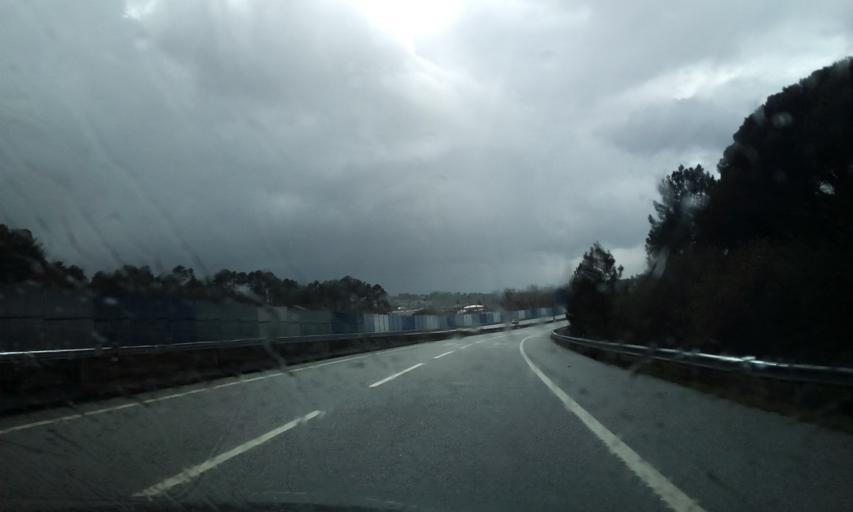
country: PT
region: Viseu
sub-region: Viseu
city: Viseu
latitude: 40.6234
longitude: -7.9122
